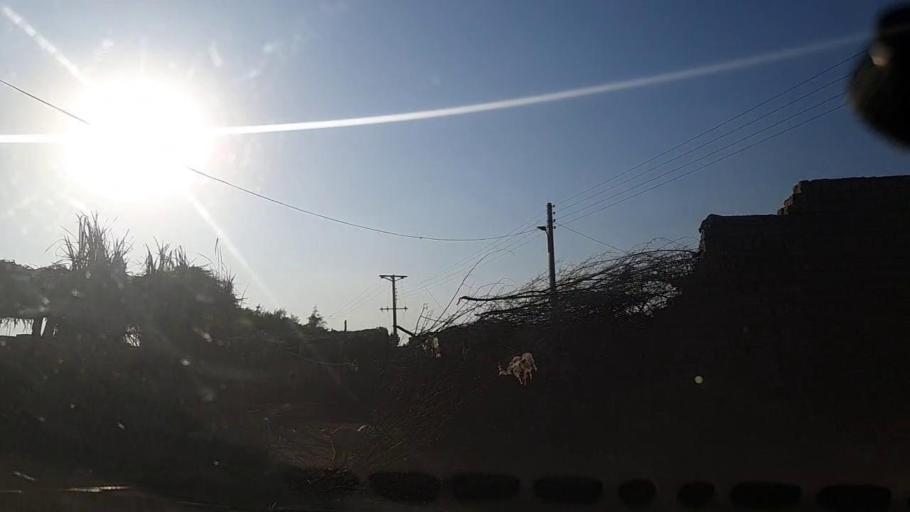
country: PK
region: Sindh
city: Berani
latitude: 25.6743
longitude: 68.9149
